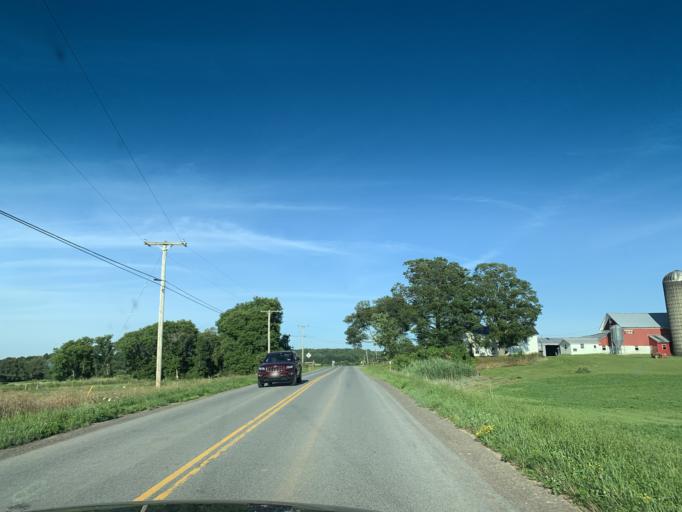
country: US
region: New York
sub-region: Oneida County
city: Vernon
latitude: 43.0558
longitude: -75.4780
